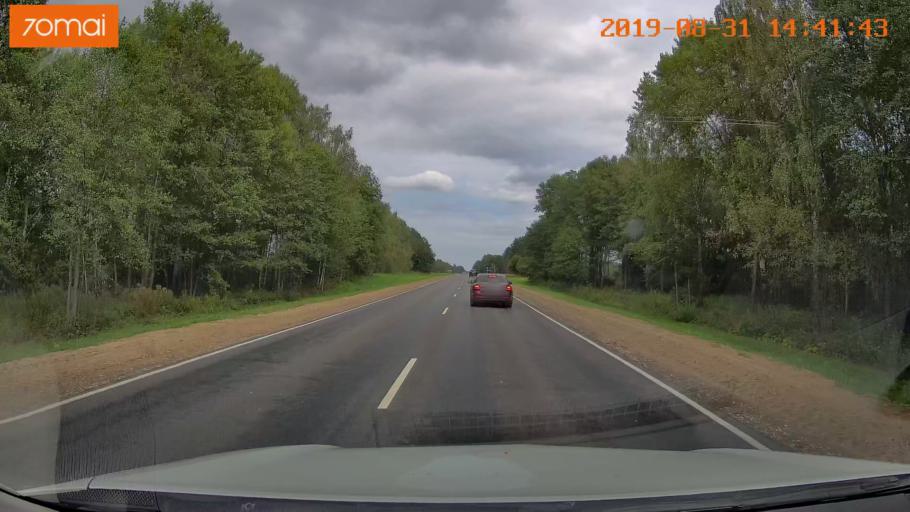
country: RU
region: Smolensk
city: Yekimovichi
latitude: 54.2043
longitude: 33.5956
